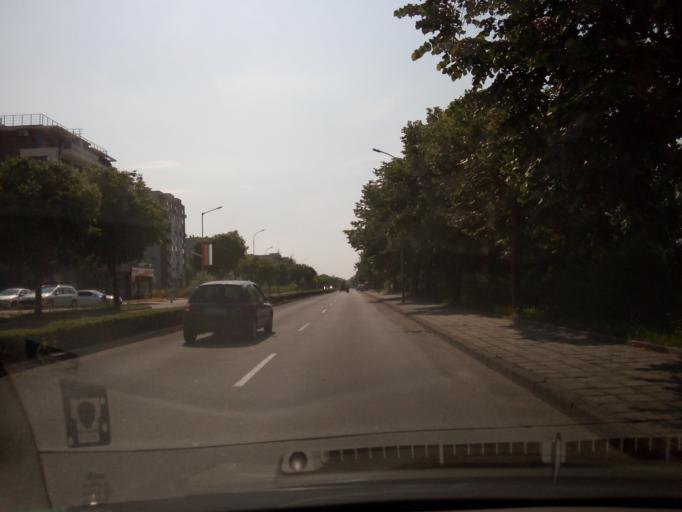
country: BG
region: Burgas
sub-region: Obshtina Pomorie
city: Pomorie
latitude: 42.5637
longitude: 27.6272
